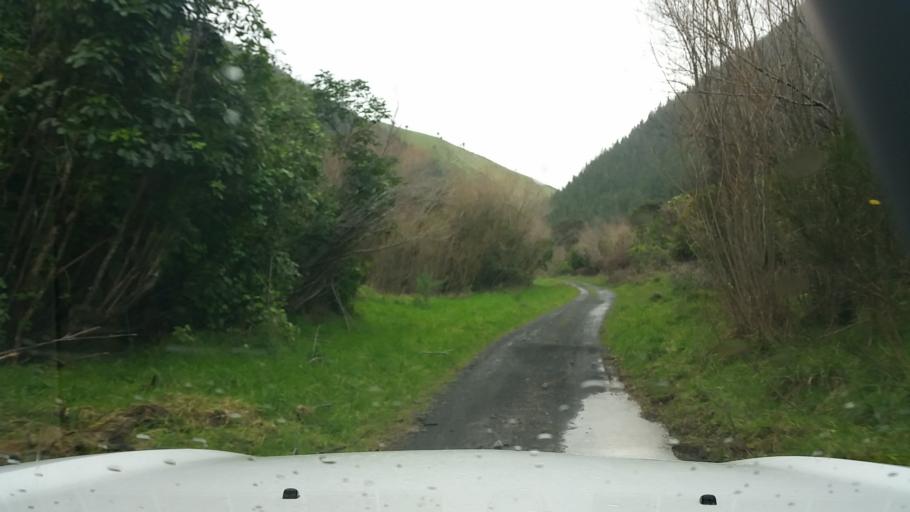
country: NZ
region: Wellington
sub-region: South Wairarapa District
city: Waipawa
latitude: -41.4095
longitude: 175.2497
